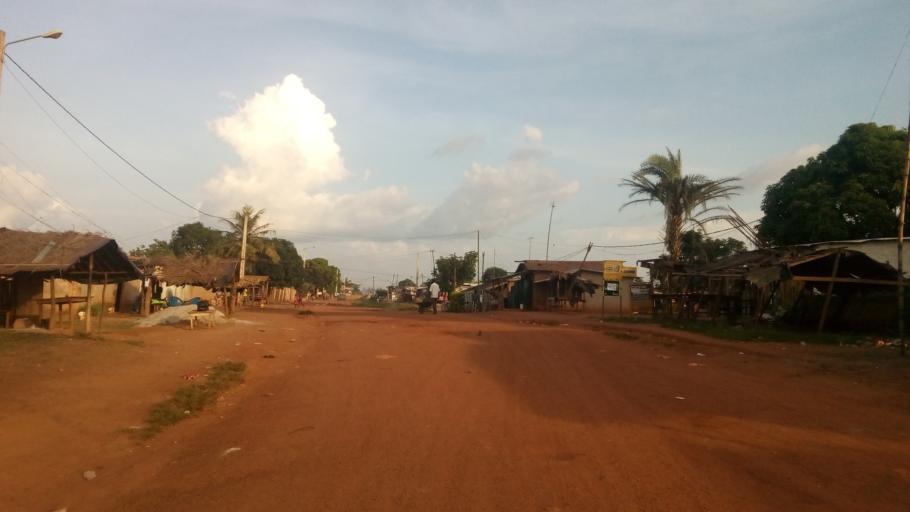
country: CI
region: Dix-Huit Montagnes
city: Duekoue
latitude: 6.7343
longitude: -7.3427
